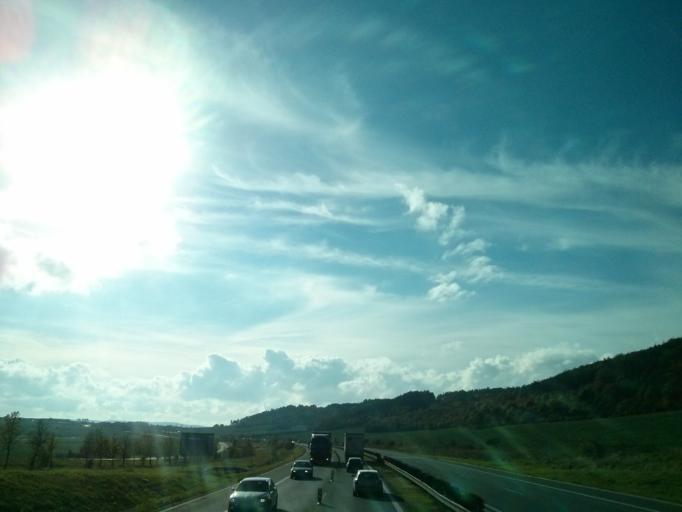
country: CZ
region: Central Bohemia
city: Zebrak
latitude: 49.8893
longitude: 13.9269
